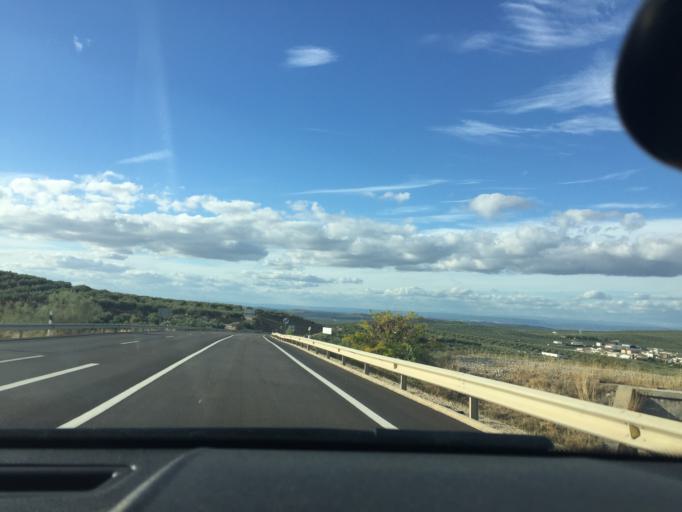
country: ES
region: Andalusia
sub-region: Provincia de Jaen
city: Torredonjimeno
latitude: 37.7569
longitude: -3.9621
